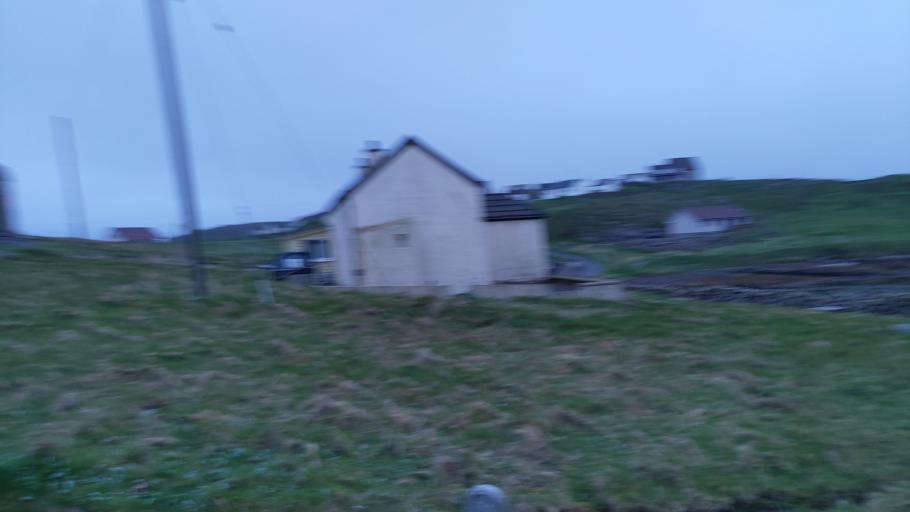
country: GB
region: Scotland
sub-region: Shetland Islands
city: Shetland
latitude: 60.4228
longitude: -0.7630
